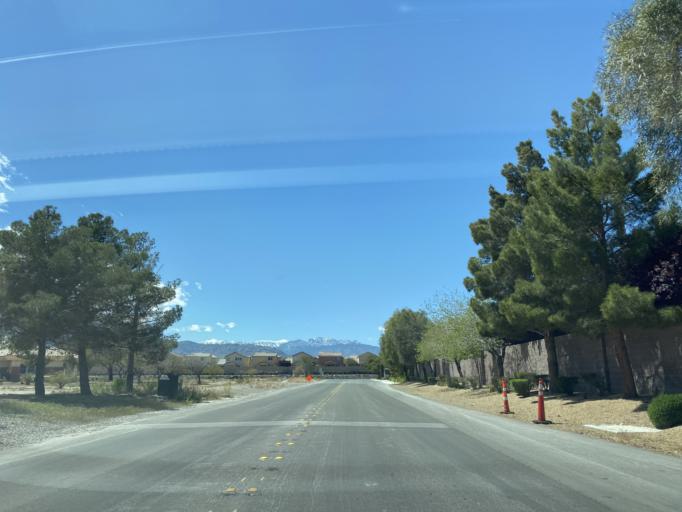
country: US
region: Nevada
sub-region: Clark County
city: North Las Vegas
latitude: 36.3091
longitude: -115.2401
